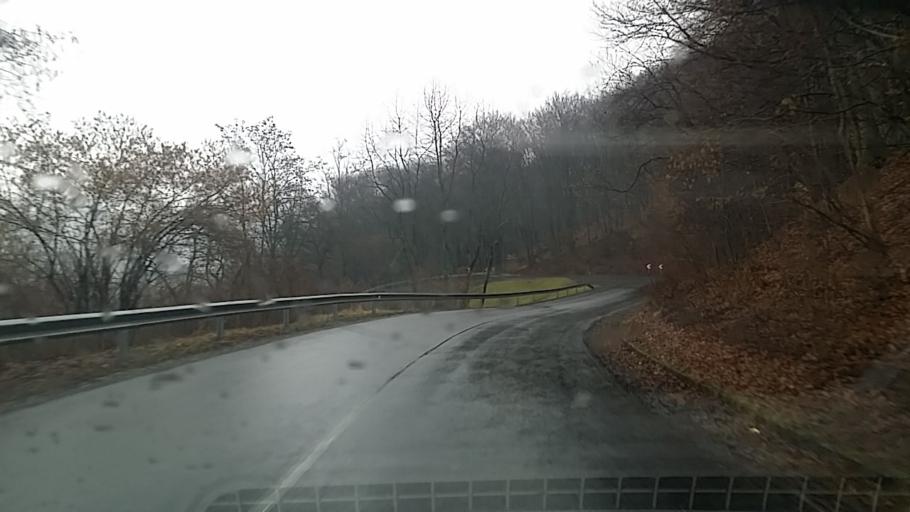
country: HU
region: Borsod-Abauj-Zemplen
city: Rudabanya
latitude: 48.4803
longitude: 20.5505
